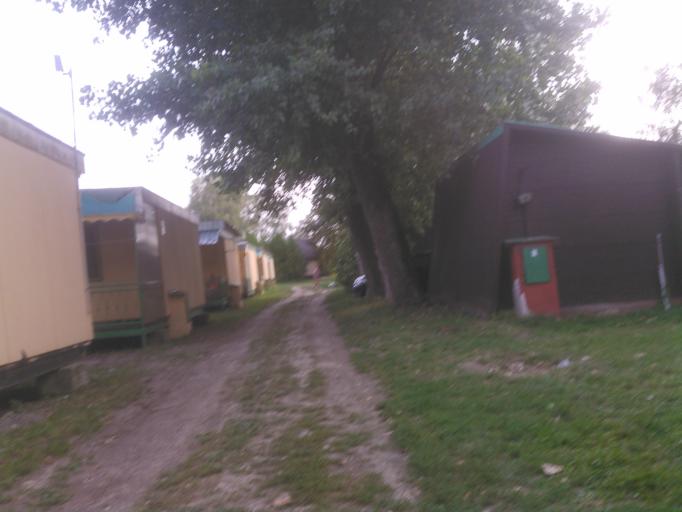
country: SK
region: Trnavsky
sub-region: Okres Galanta
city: Galanta
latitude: 48.1347
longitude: 17.7859
